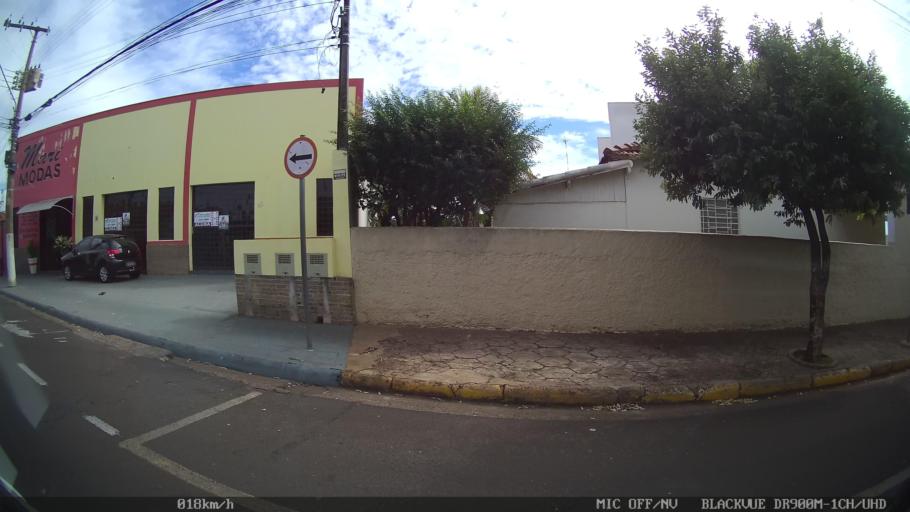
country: BR
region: Sao Paulo
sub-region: Catanduva
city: Catanduva
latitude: -21.1459
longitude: -48.9661
